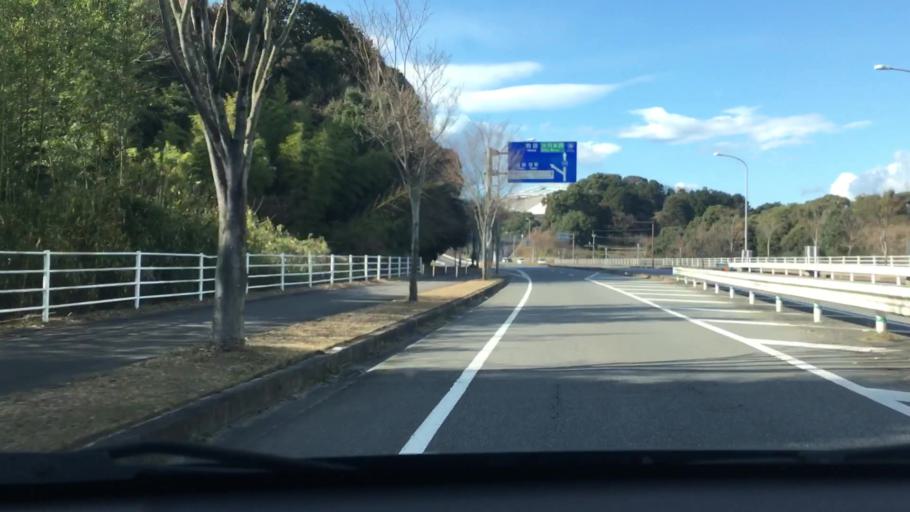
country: JP
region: Oita
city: Tsurusaki
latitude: 33.1939
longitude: 131.6659
